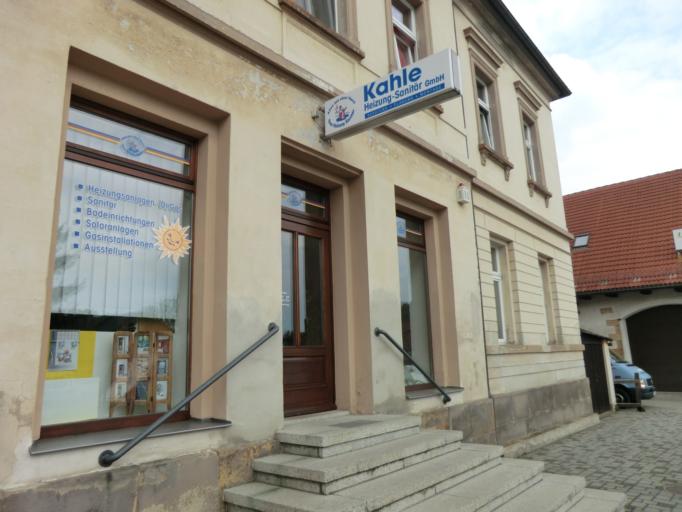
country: DE
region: Saxony
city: Grossschonau
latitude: 50.8974
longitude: 14.6669
